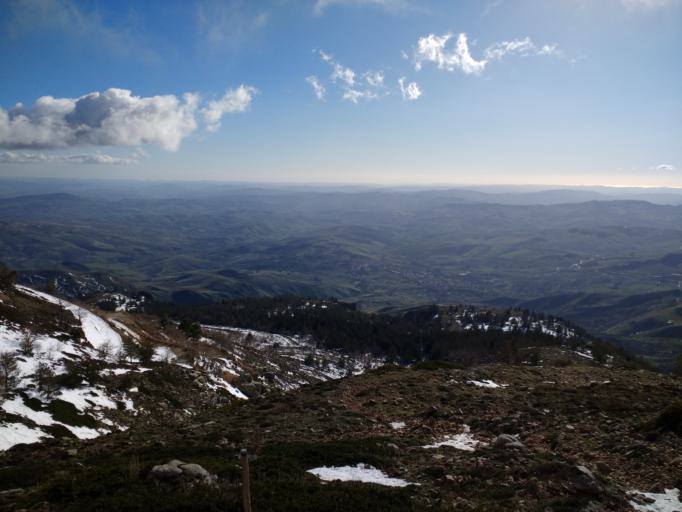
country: IT
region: Sicily
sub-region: Palermo
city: Castellana Sicula
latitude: 37.8292
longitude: 14.0480
